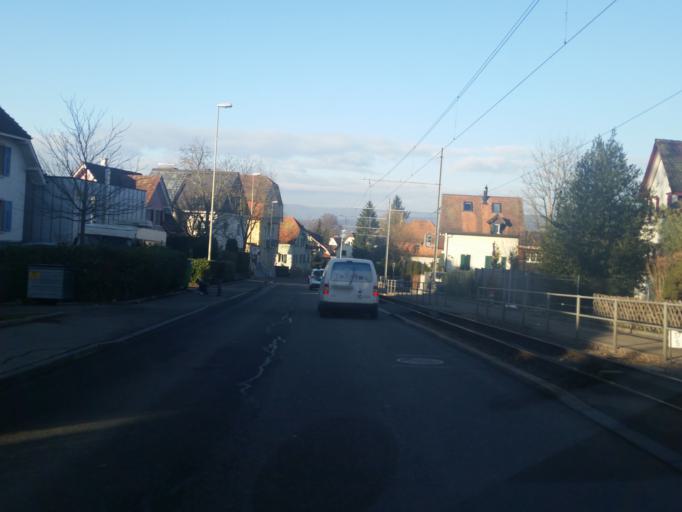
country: CH
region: Zurich
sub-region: Bezirk Dietikon
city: Dietikon / Kreuzacker
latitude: 47.3951
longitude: 8.3988
